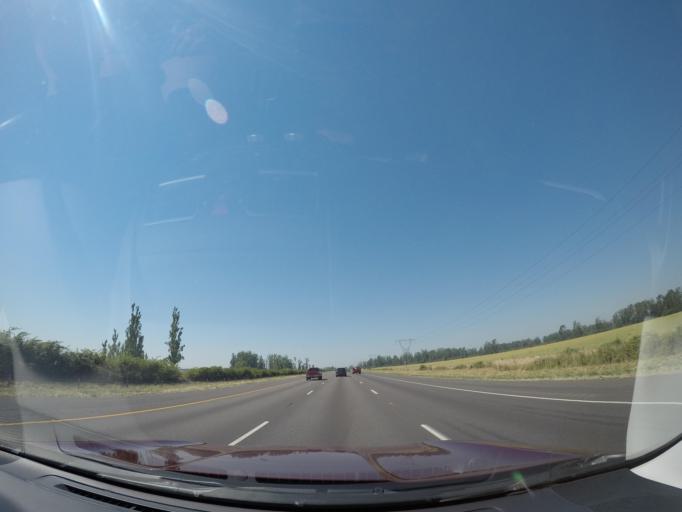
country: US
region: Oregon
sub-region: Marion County
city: Gervais
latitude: 45.1138
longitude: -122.9189
